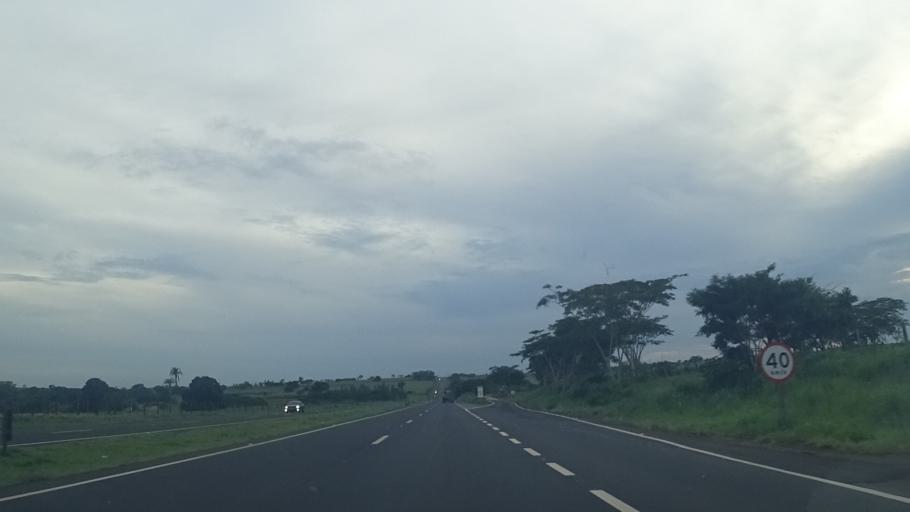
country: BR
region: Sao Paulo
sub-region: Martinopolis
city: Martinopolis
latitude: -22.1382
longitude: -51.2177
